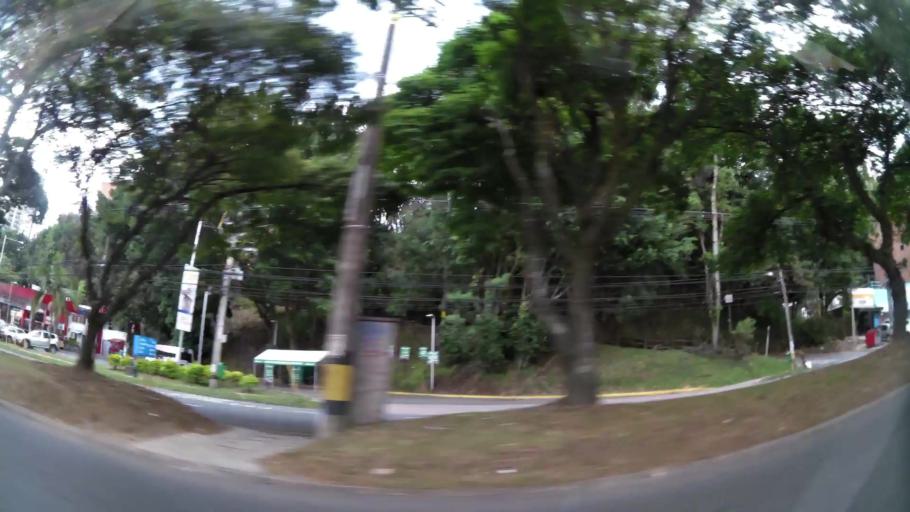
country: CO
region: Antioquia
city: Medellin
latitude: 6.2238
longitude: -75.5693
